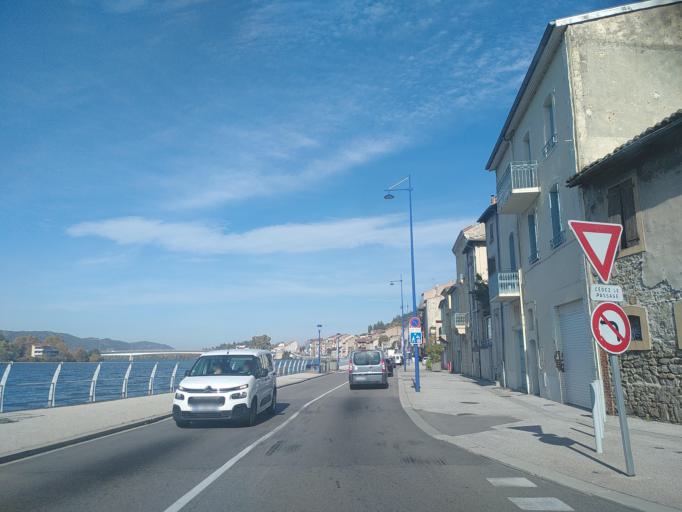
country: FR
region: Rhone-Alpes
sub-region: Departement de la Drome
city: Saint-Vallier
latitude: 45.1781
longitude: 4.8132
